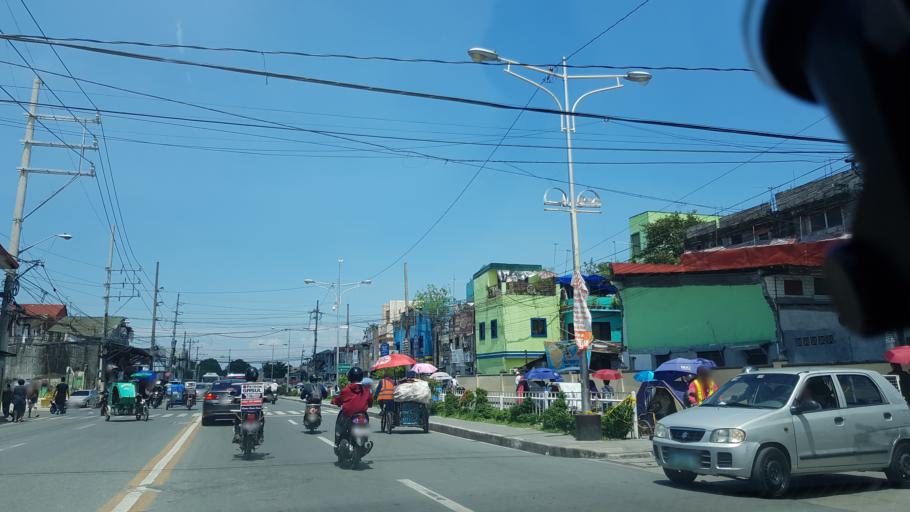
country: PH
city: Sambayanihan People's Village
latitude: 14.4601
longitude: 120.9948
